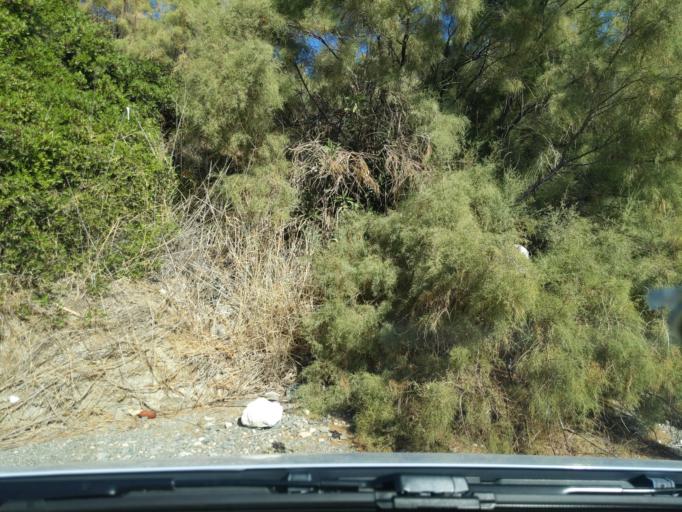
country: GR
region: Crete
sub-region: Nomos Irakleiou
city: Moires
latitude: 34.9385
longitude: 24.8129
